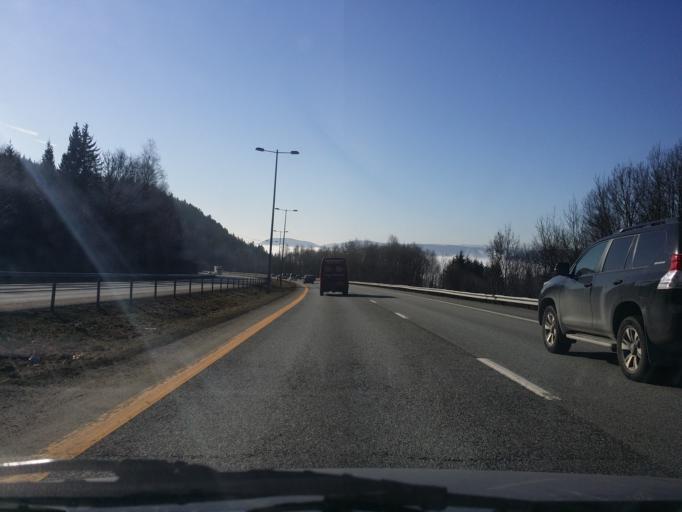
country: NO
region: Buskerud
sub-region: Lier
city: Tranby
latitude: 59.8001
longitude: 10.2681
